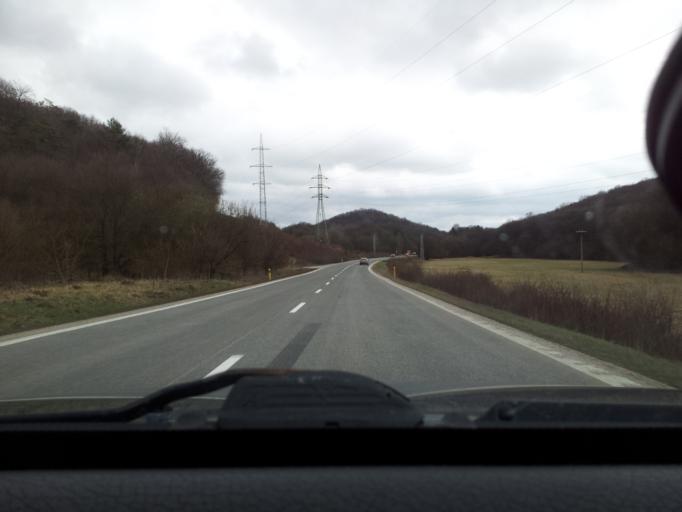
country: SK
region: Kosicky
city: Roznava
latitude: 48.6144
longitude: 20.6333
